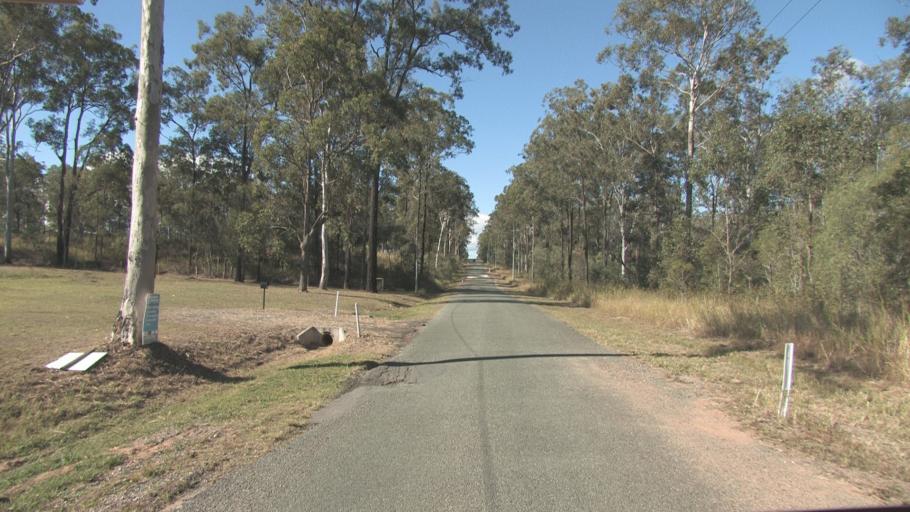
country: AU
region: Queensland
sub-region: Logan
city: Chambers Flat
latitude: -27.7982
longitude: 153.0742
